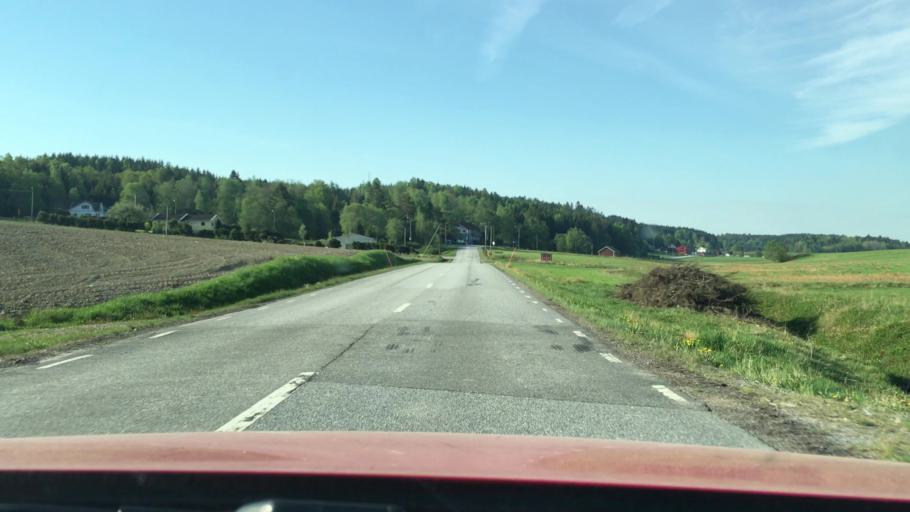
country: SE
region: Vaestra Goetaland
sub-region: Munkedals Kommun
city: Munkedal
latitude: 58.6081
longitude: 11.5589
